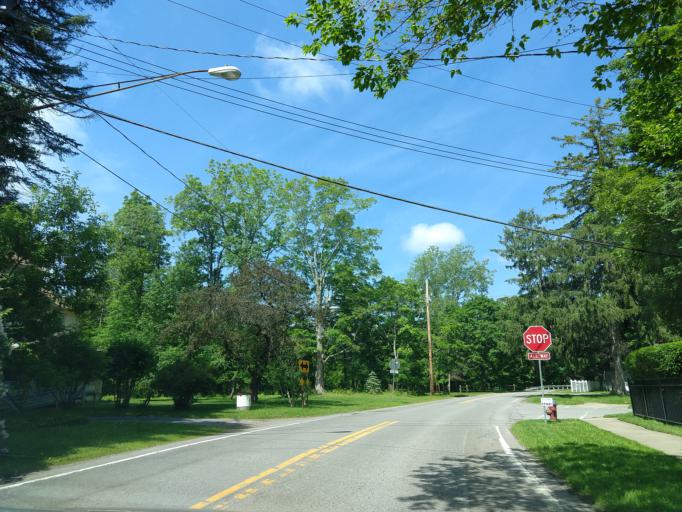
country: US
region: New York
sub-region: Erie County
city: East Aurora
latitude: 42.7578
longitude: -78.6225
